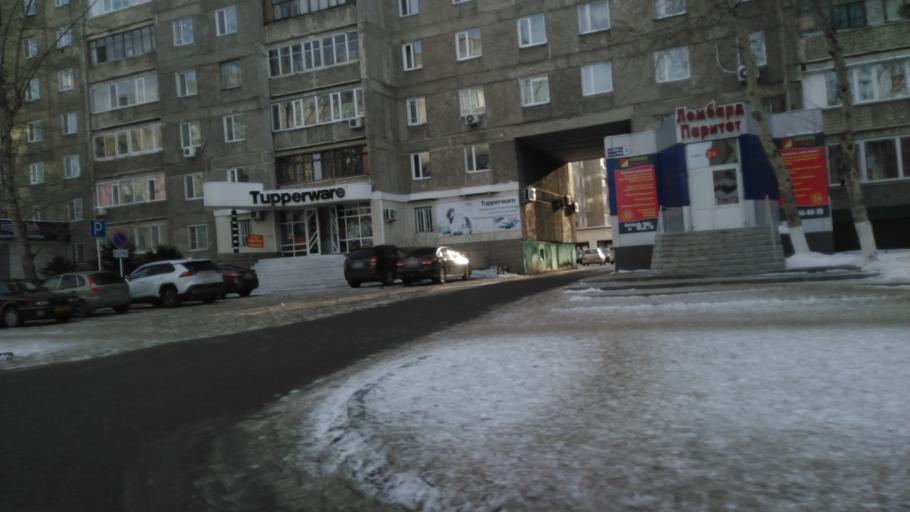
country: KZ
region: Pavlodar
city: Pavlodar
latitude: 52.2677
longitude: 76.9516
